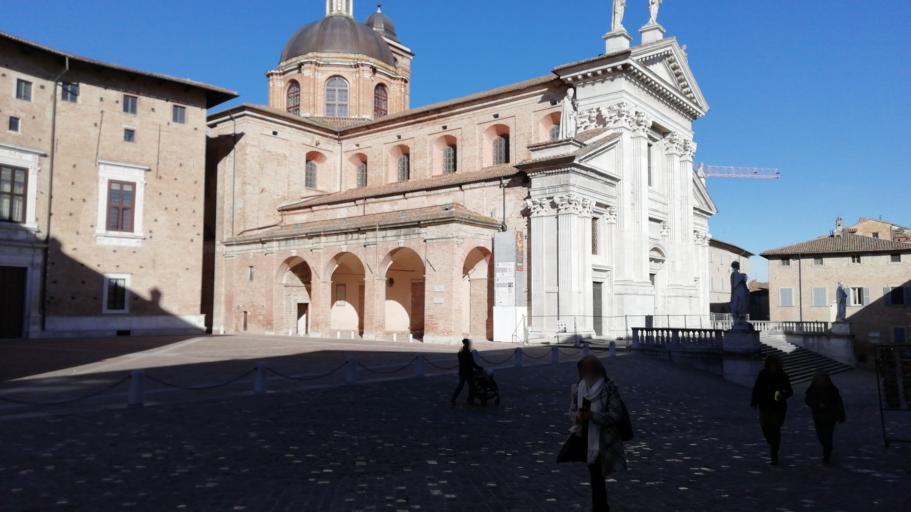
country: IT
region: The Marches
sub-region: Provincia di Pesaro e Urbino
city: Urbino
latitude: 43.7243
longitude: 12.6371
